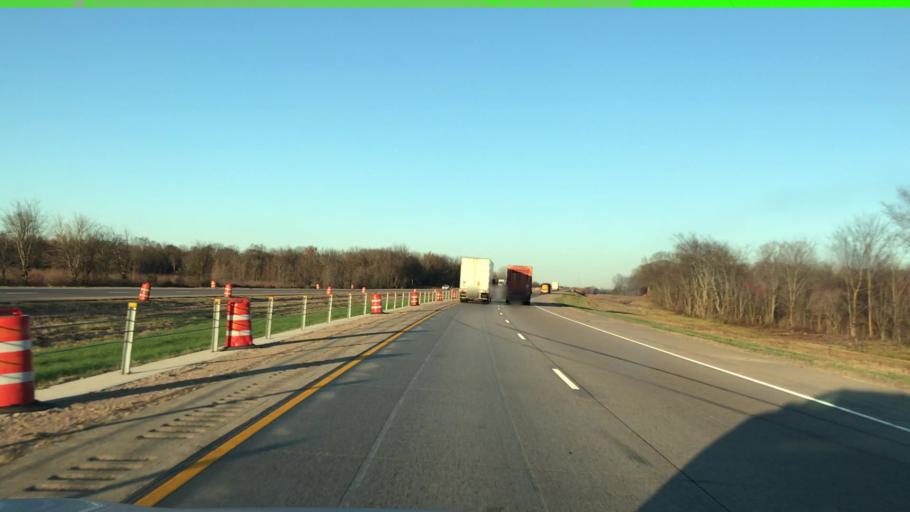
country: US
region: Arkansas
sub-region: Miller County
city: Texarkana
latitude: 33.5848
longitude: -93.8407
